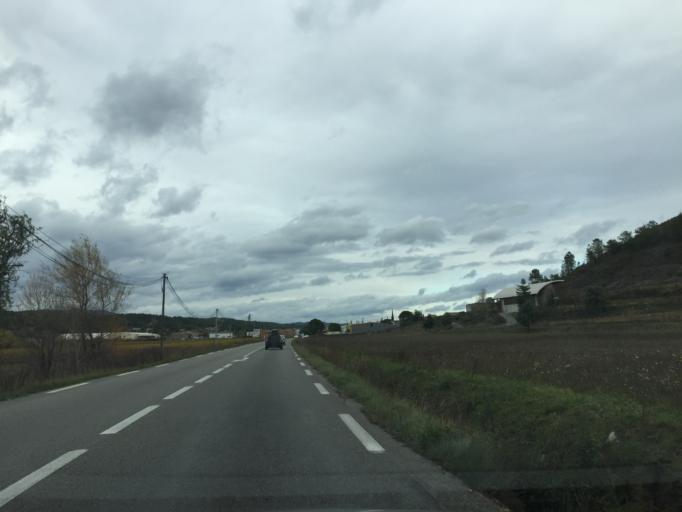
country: FR
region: Rhone-Alpes
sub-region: Departement de l'Ardeche
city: Rosieres
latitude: 44.4860
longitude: 4.2694
